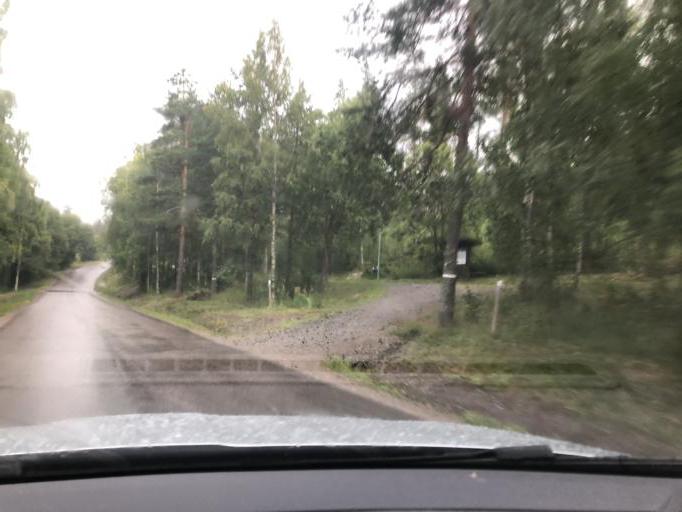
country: SE
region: Vaesternorrland
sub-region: Sundsvalls Kommun
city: Sundsvall
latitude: 62.4056
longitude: 17.3013
